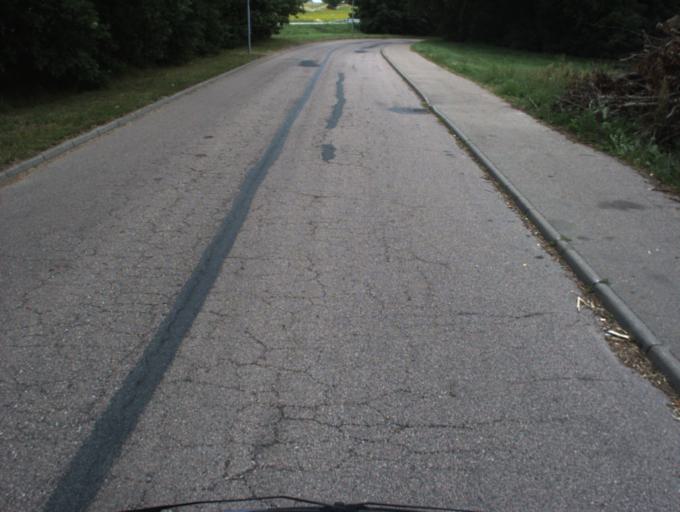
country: SE
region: Skane
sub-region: Helsingborg
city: Rydeback
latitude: 56.0080
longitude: 12.7621
